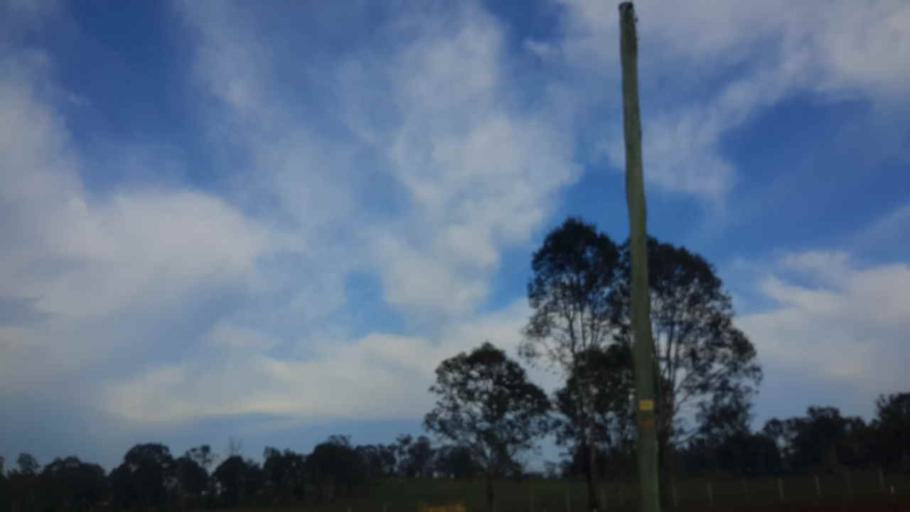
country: AU
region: New South Wales
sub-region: Liverpool
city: Bringelly
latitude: -33.9543
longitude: 150.7395
